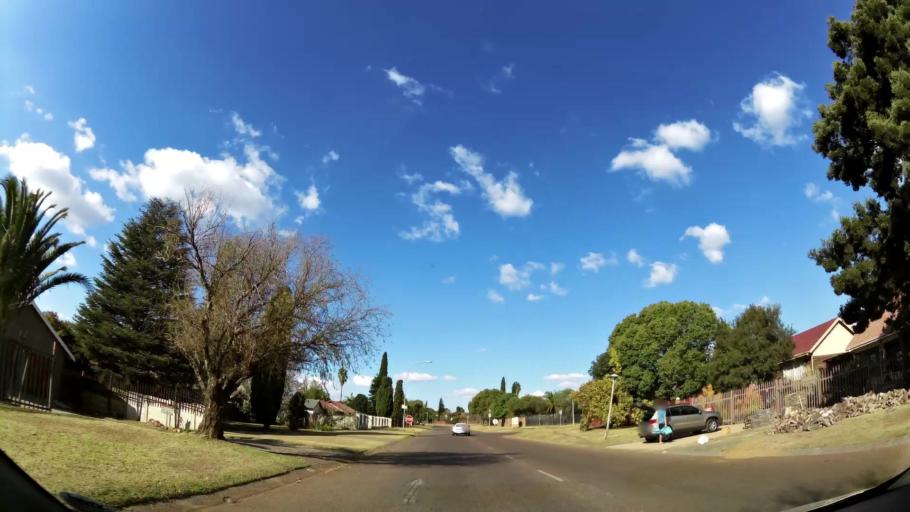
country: ZA
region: Mpumalanga
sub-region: Nkangala District Municipality
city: Witbank
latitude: -25.8966
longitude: 29.2472
